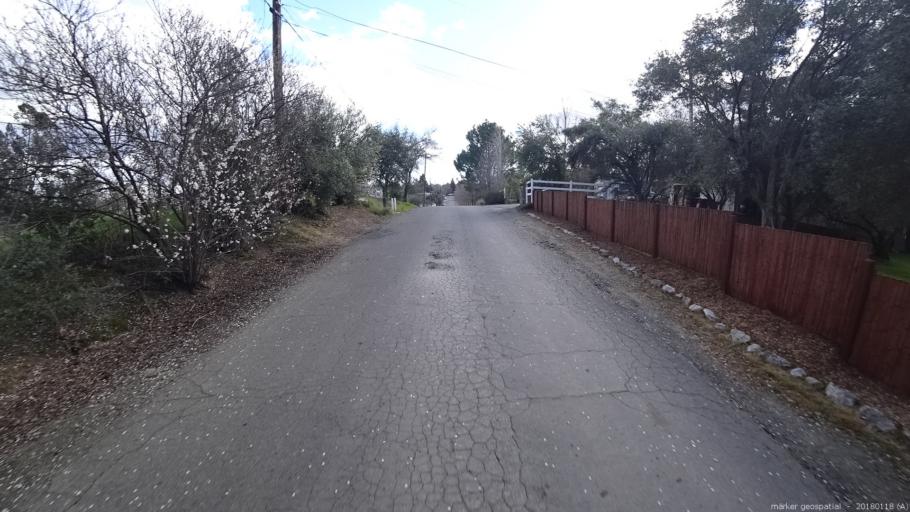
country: US
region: California
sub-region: Sacramento County
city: Orangevale
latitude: 38.7029
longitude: -121.2066
